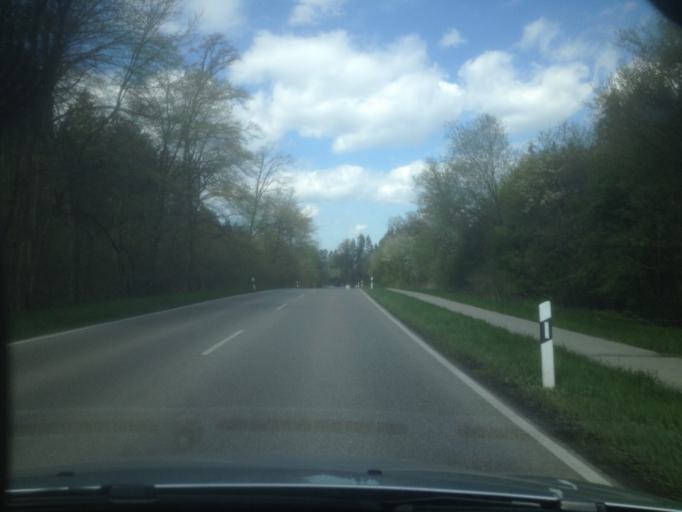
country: DE
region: Bavaria
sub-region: Swabia
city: Adelsried
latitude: 48.3860
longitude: 10.7380
